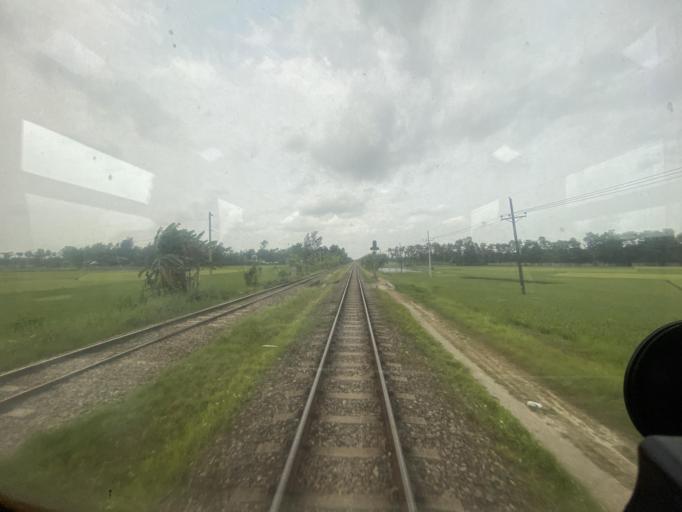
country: BD
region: Chittagong
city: Laksham
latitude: 23.2039
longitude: 91.1556
